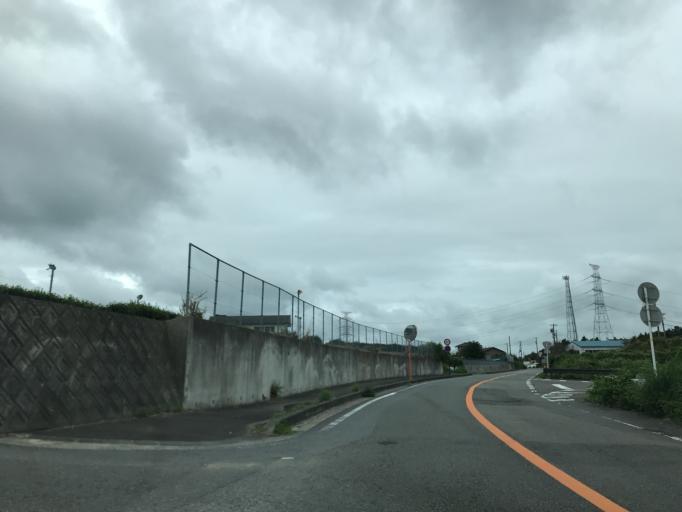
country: JP
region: Shizuoka
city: Kanaya
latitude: 34.7719
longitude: 138.1407
